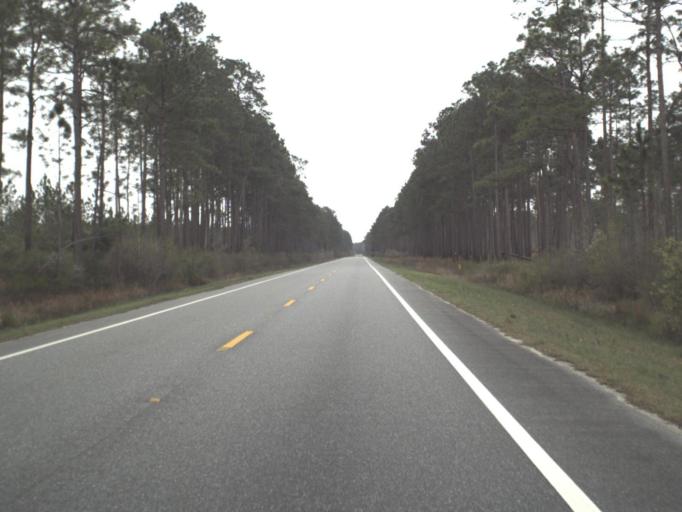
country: US
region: Florida
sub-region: Franklin County
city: Apalachicola
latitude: 29.8675
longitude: -84.9747
